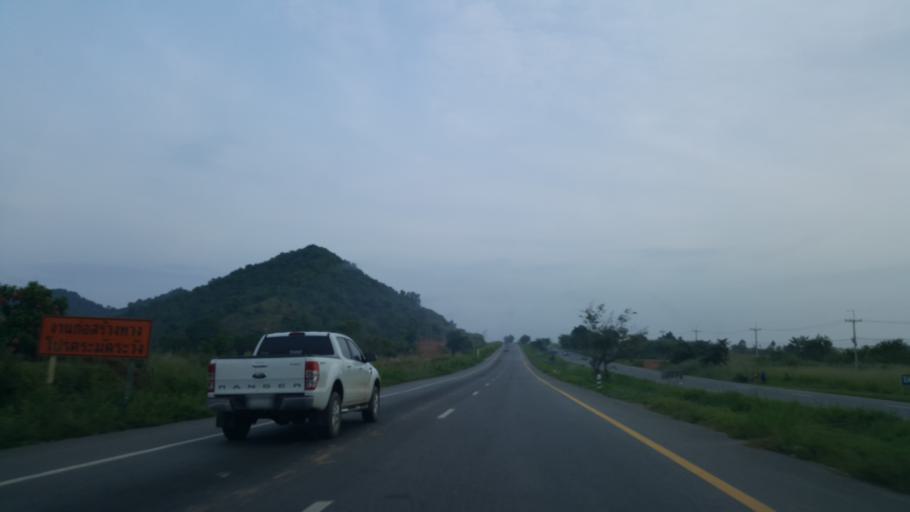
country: TH
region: Rayong
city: Ban Chang
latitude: 12.7473
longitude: 100.9910
